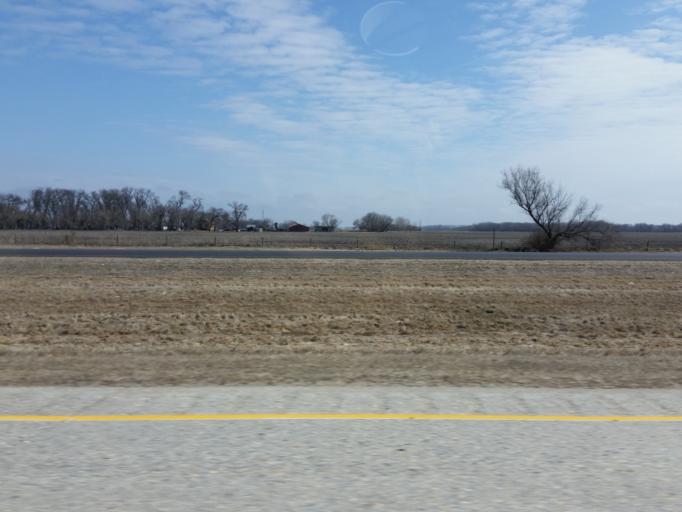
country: US
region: North Dakota
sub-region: Richland County
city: Wahpeton
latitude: 46.0346
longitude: -96.8356
